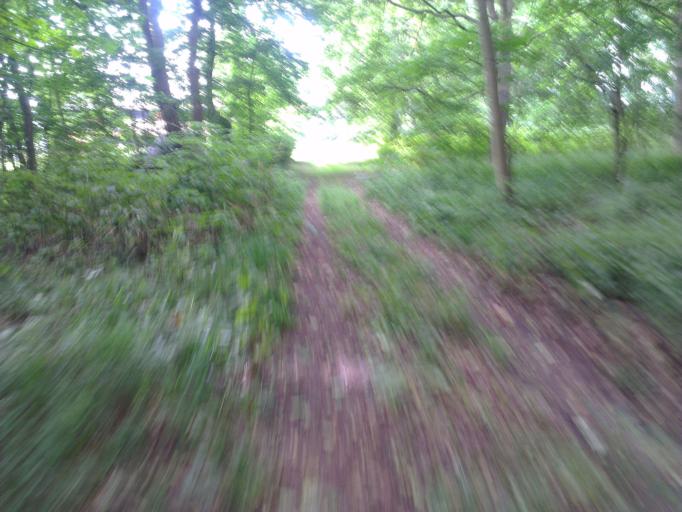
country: DK
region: Capital Region
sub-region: Frederikssund Kommune
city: Jaegerspris
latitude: 55.8896
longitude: 12.0028
